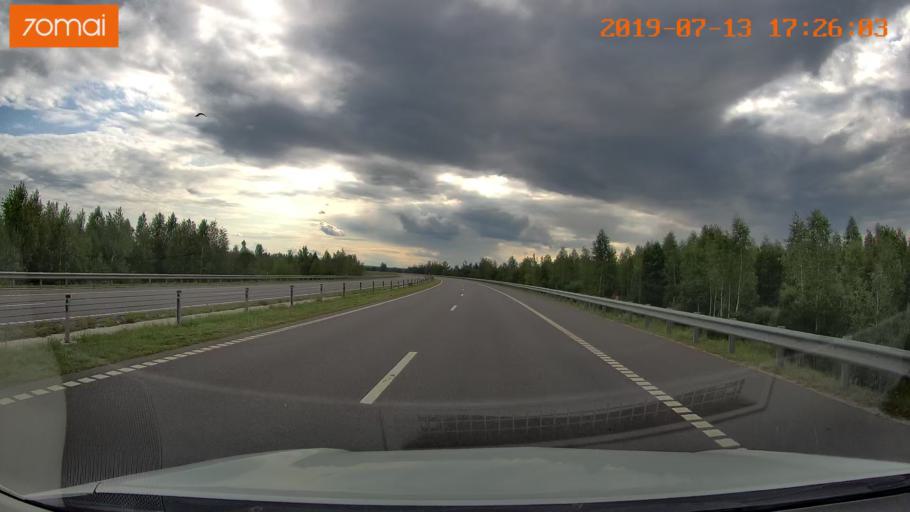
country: BY
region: Mogilev
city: Babruysk
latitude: 53.2560
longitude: 29.1926
